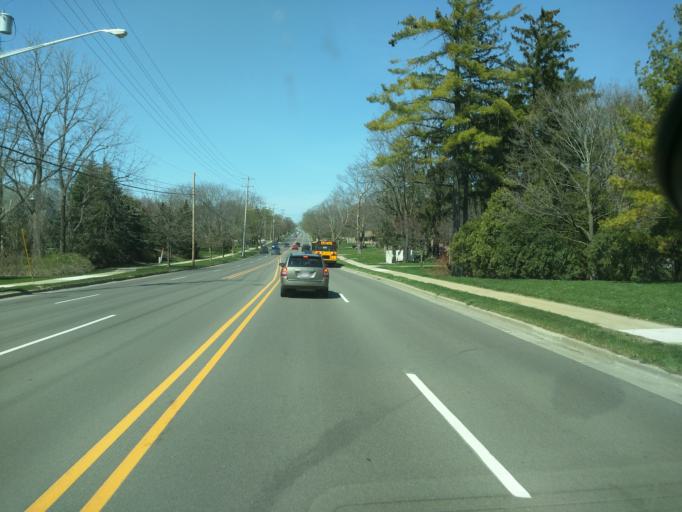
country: US
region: Michigan
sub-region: Kent County
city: East Grand Rapids
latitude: 42.9270
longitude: -85.5895
